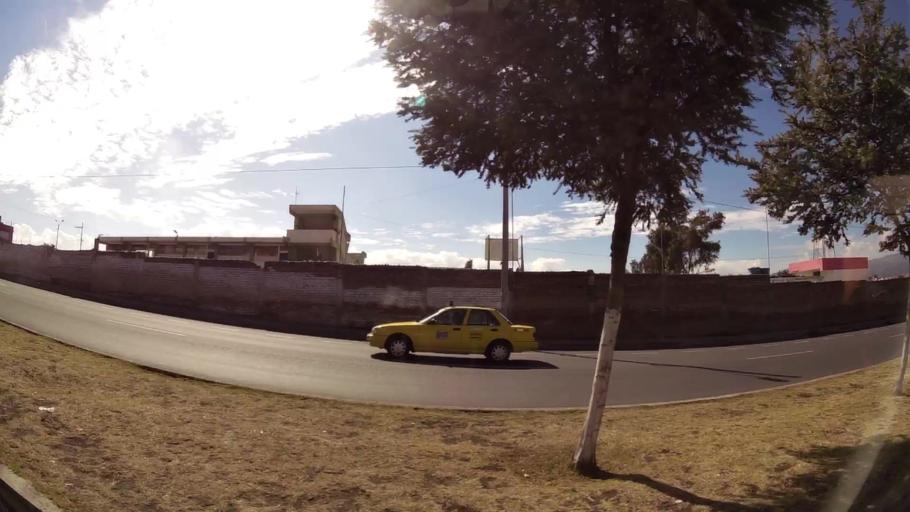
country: EC
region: Chimborazo
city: Riobamba
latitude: -1.6566
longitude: -78.6712
